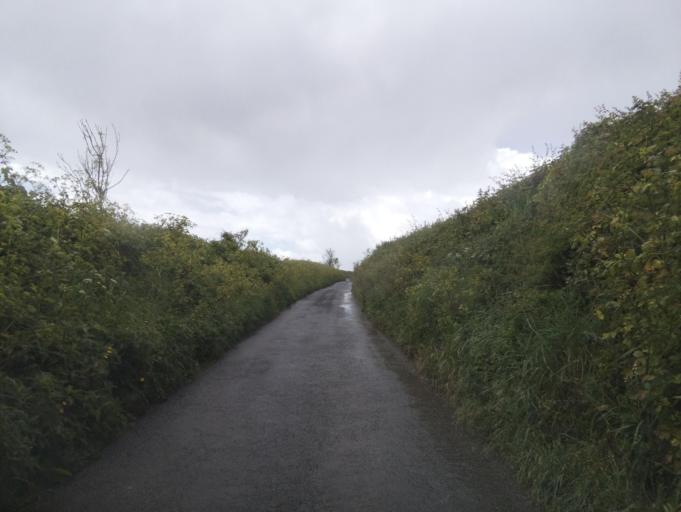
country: GB
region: England
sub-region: Devon
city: Dartmouth
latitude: 50.3542
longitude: -3.5535
